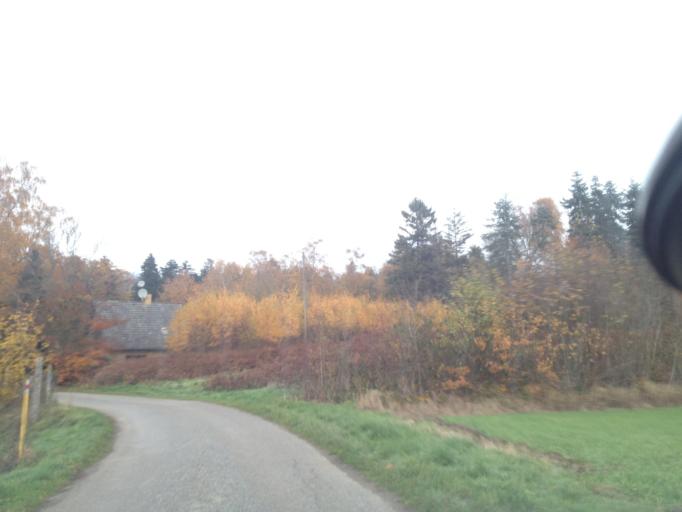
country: DK
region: South Denmark
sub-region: Assens Kommune
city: Vissenbjerg
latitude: 55.4240
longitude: 10.1657
